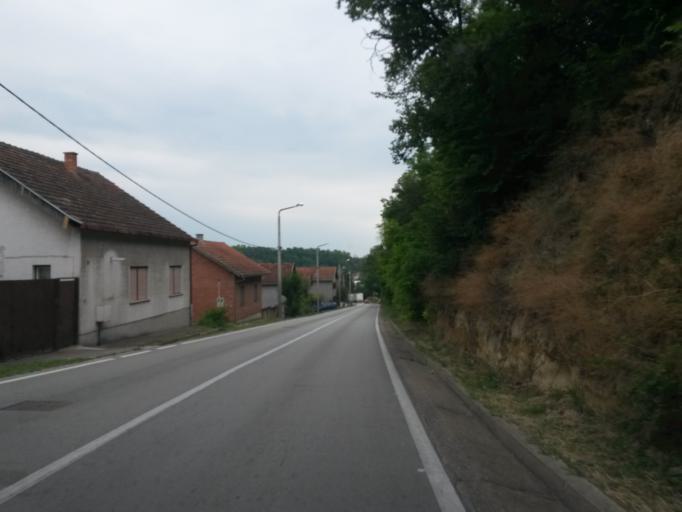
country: HR
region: Vukovarsko-Srijemska
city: Lovas
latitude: 45.2491
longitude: 19.2208
